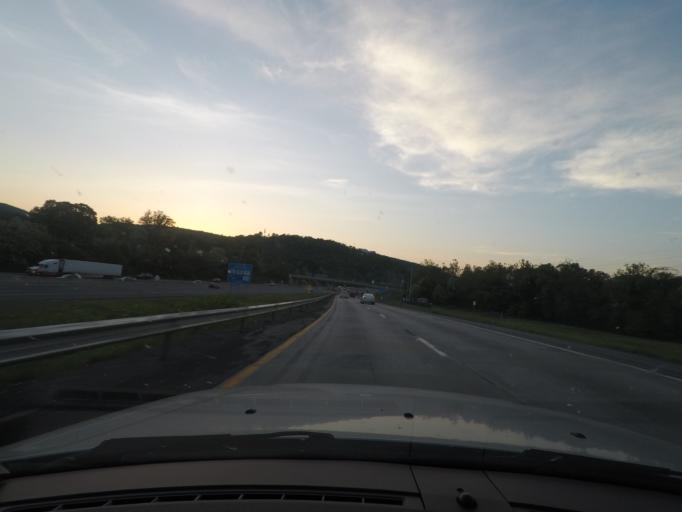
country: US
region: New York
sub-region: Rockland County
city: Suffern
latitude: 41.1231
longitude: -74.1634
